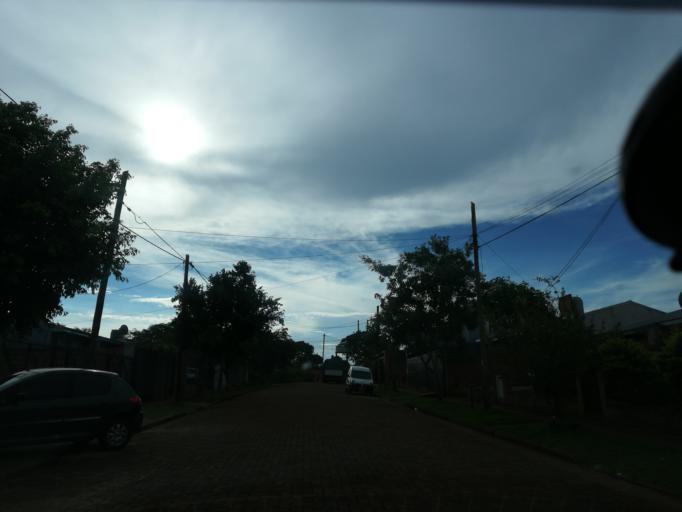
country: AR
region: Misiones
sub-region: Departamento de Capital
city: Posadas
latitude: -27.4188
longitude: -55.9246
